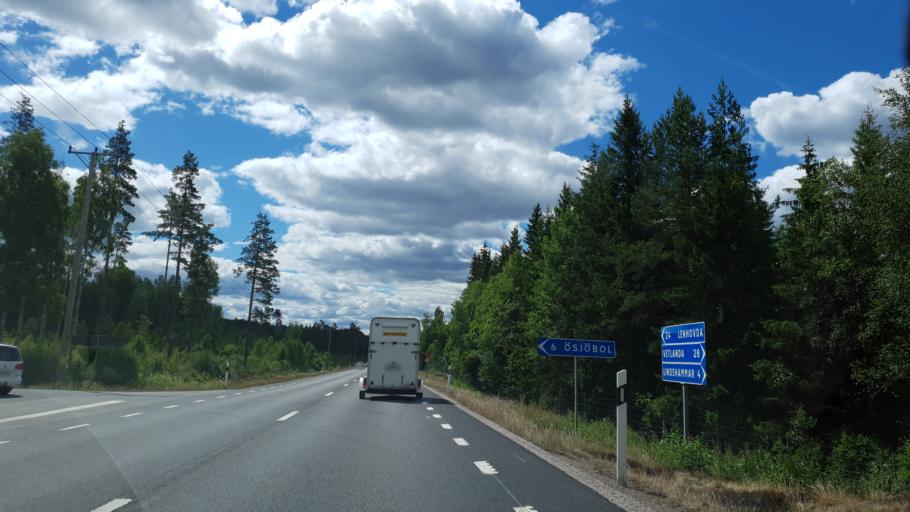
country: SE
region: Kronoberg
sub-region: Vaxjo Kommun
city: Braas
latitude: 57.1914
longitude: 15.1562
